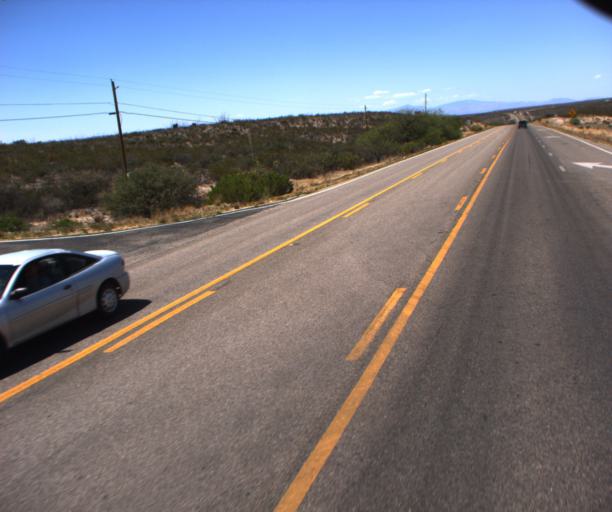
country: US
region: Arizona
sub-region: Cochise County
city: Tombstone
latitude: 31.7233
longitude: -110.0735
